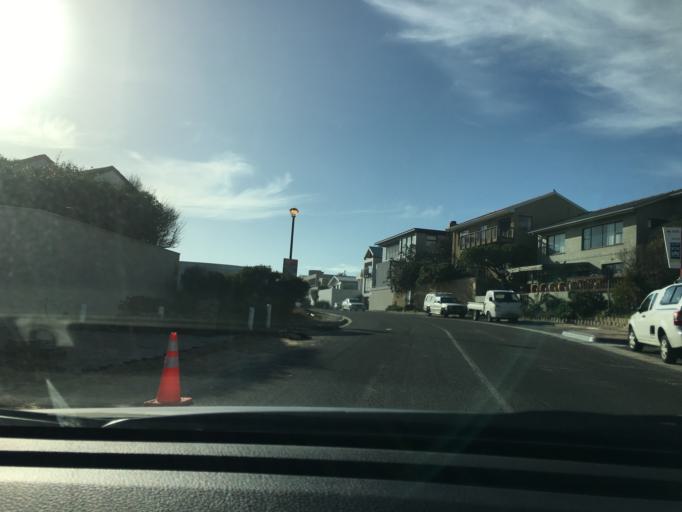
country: ZA
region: Western Cape
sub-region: City of Cape Town
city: Sunset Beach
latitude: -33.7971
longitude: 18.4599
